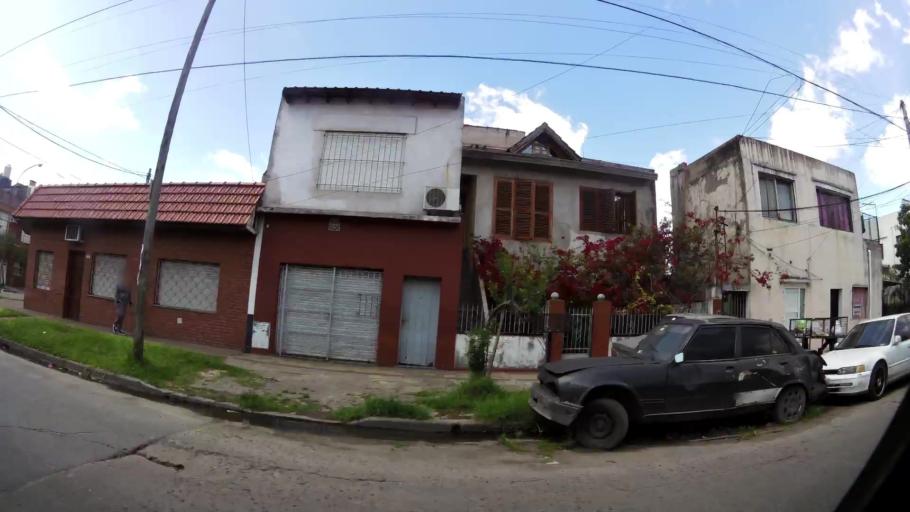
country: AR
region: Buenos Aires
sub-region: Partido de Lanus
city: Lanus
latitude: -34.6944
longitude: -58.4213
